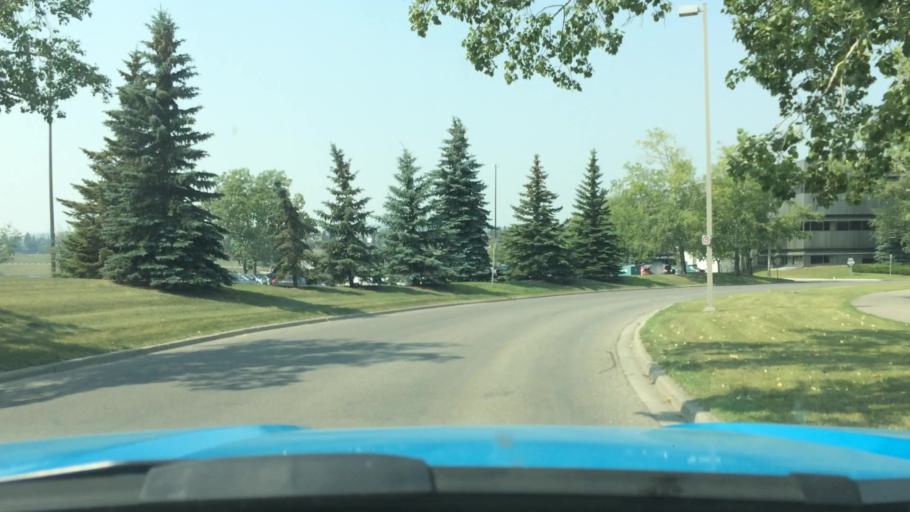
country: CA
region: Alberta
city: Calgary
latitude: 51.1122
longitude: -114.0436
